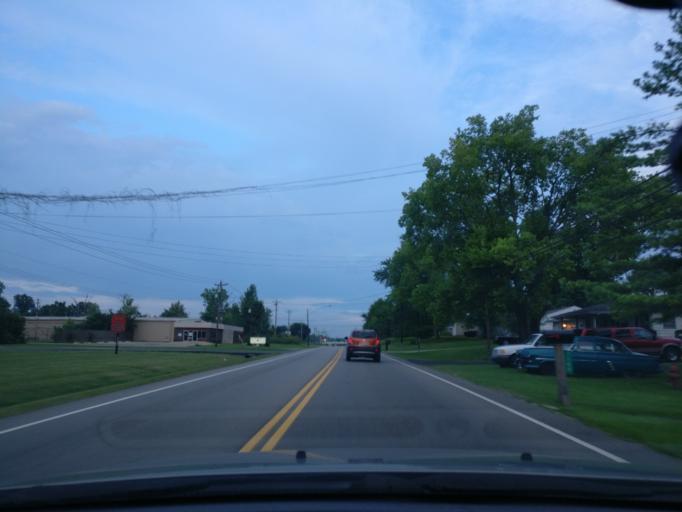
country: US
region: Ohio
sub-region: Warren County
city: Franklin
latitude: 39.5473
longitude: -84.2960
